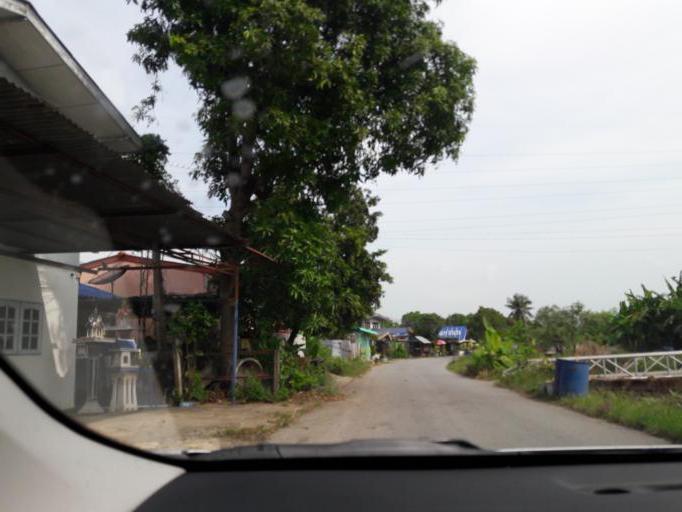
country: TH
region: Ang Thong
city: Ang Thong
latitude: 14.5807
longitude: 100.4751
